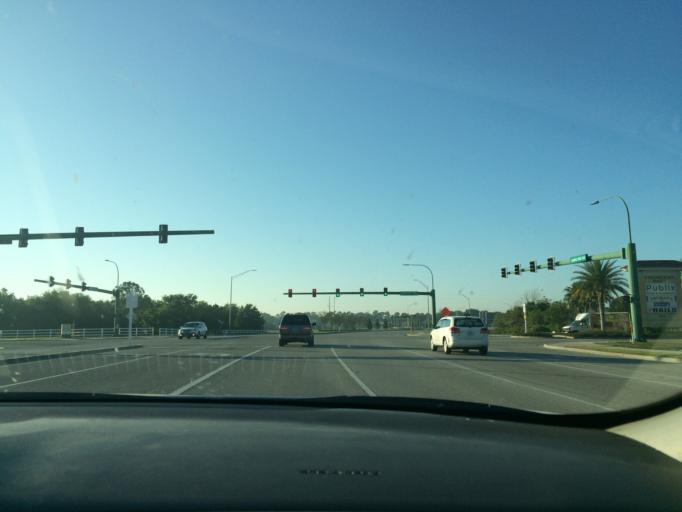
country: US
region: Florida
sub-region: Sarasota County
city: The Meadows
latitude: 27.4366
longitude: -82.4292
